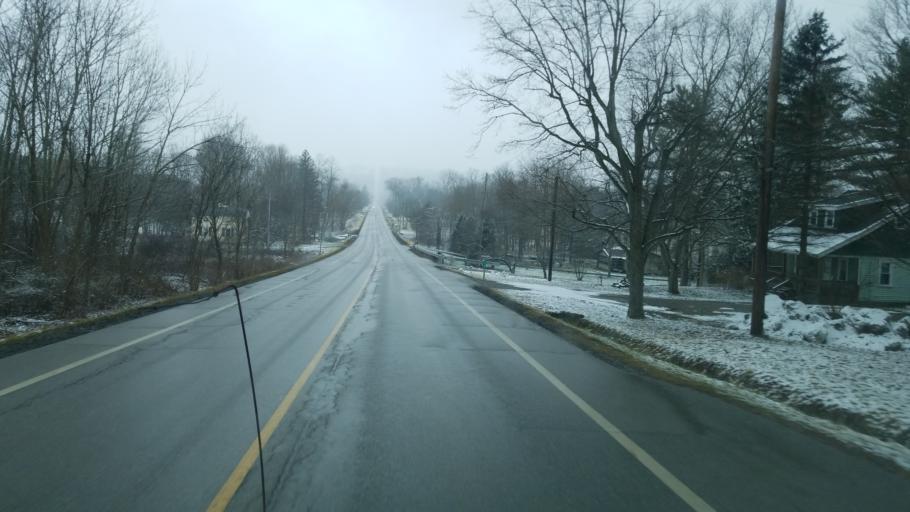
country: US
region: Ohio
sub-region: Portage County
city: Hiram
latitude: 41.3104
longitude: -81.1826
